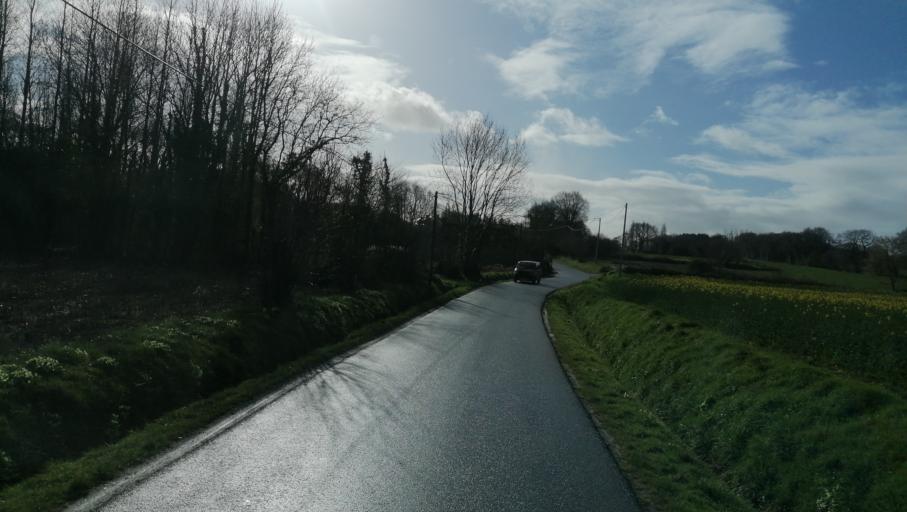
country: FR
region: Brittany
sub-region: Departement des Cotes-d'Armor
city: Plouha
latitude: 48.6534
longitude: -2.9114
